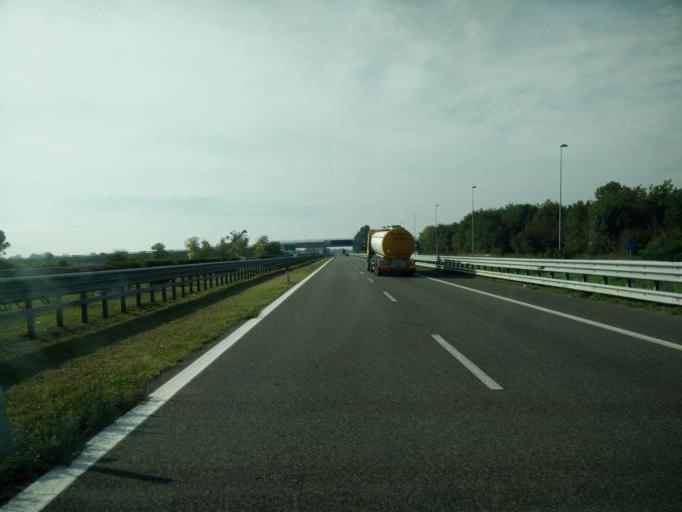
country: IT
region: Lombardy
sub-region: Provincia di Cremona
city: Battaglione-Bagnara
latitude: 45.1272
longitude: 10.0652
